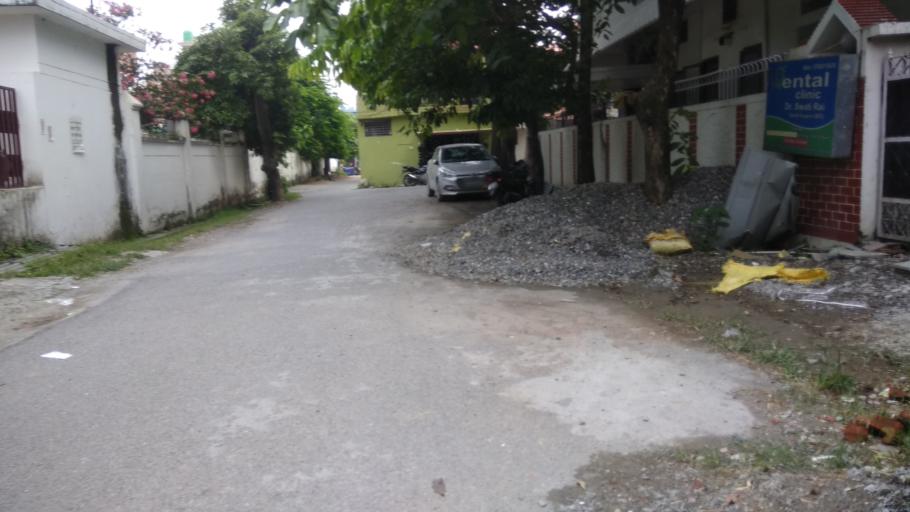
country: IN
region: Uttarakhand
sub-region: Dehradun
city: Raipur
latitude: 30.3130
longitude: 78.0627
